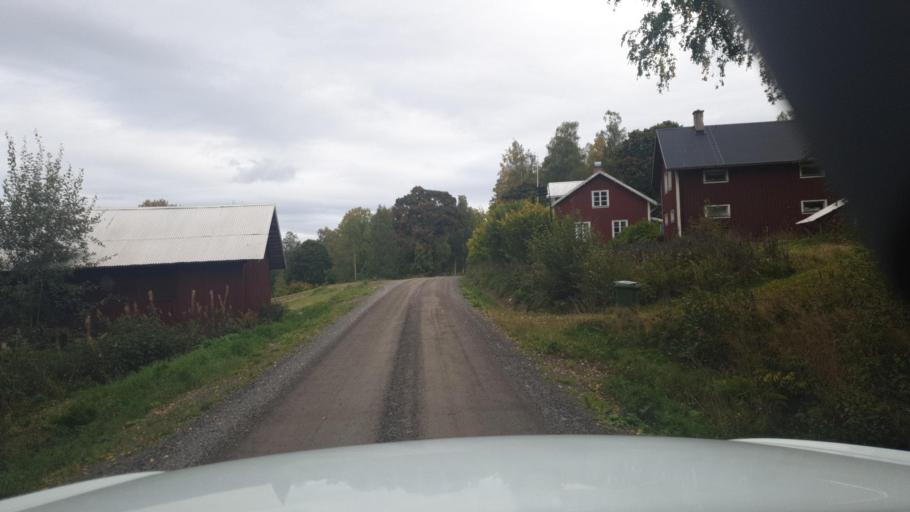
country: SE
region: Vaermland
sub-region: Torsby Kommun
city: Torsby
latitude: 59.9759
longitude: 12.8532
